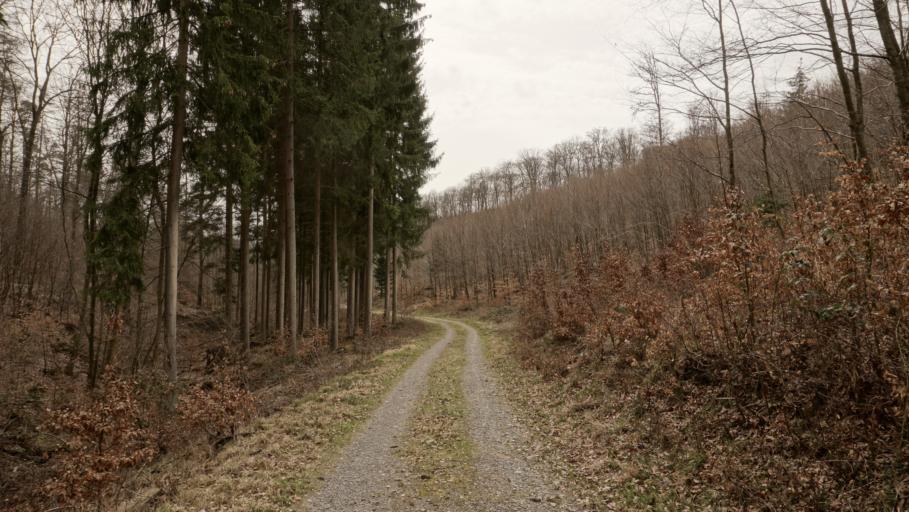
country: DE
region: Baden-Wuerttemberg
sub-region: Karlsruhe Region
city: Fahrenbach
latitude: 49.4382
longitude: 9.1273
